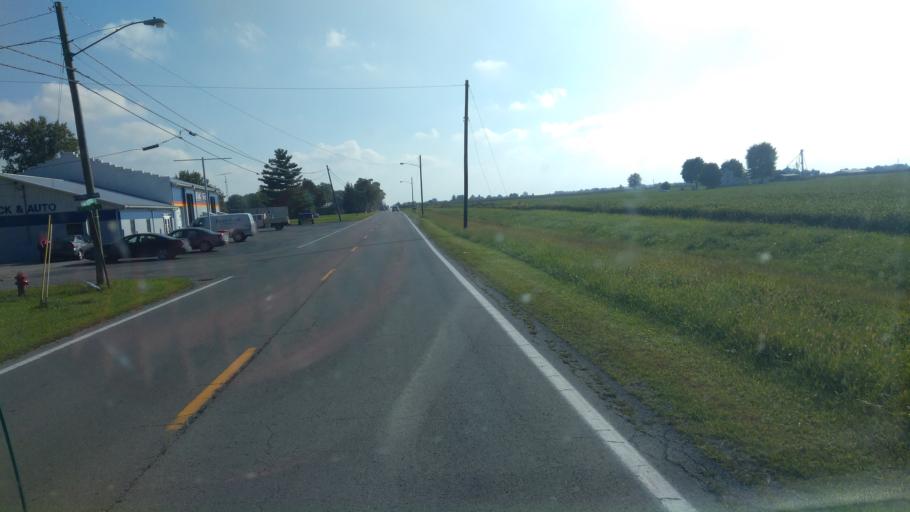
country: US
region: Ohio
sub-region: Hardin County
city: Forest
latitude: 40.7979
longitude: -83.5149
